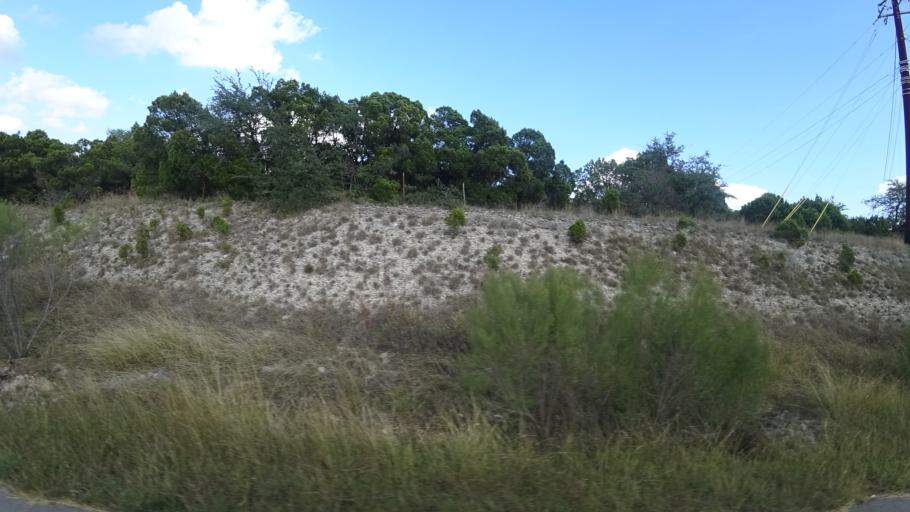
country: US
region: Texas
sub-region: Travis County
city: Barton Creek
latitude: 30.2631
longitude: -97.8888
